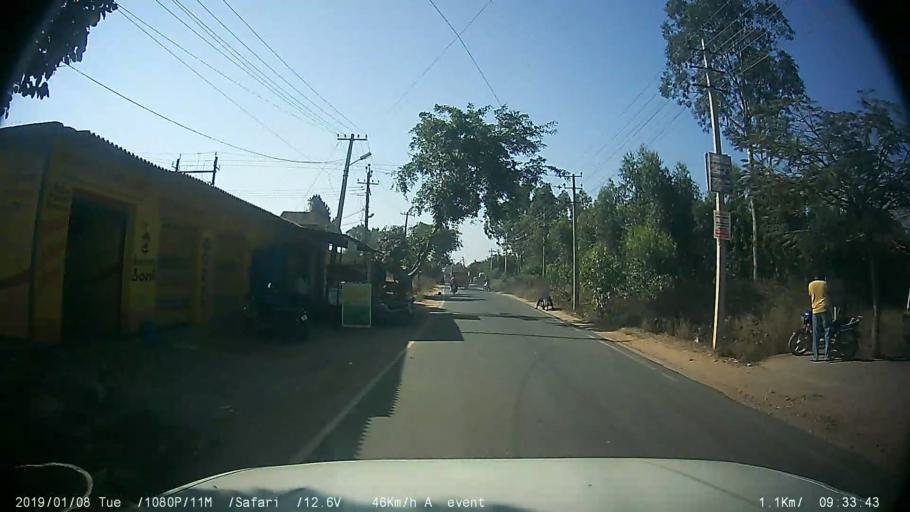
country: IN
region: Karnataka
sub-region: Bangalore Urban
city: Anekal
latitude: 12.8214
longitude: 77.6512
